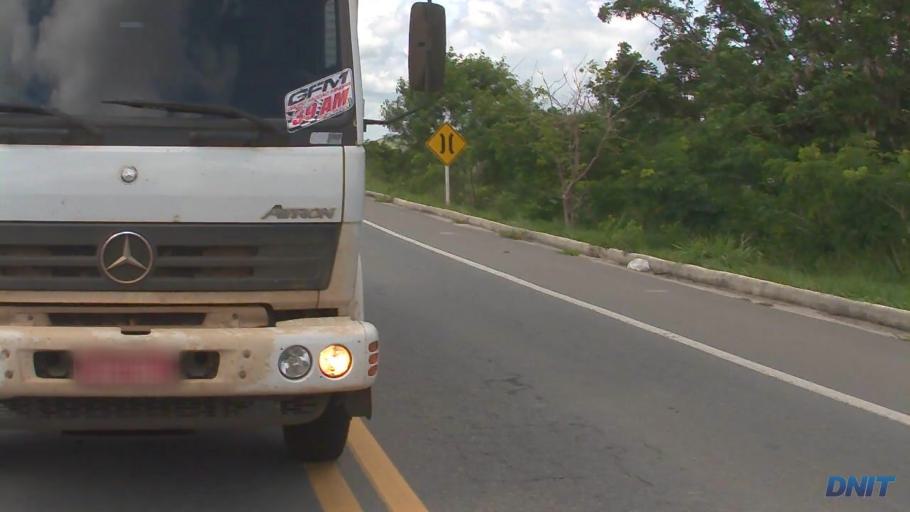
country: BR
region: Minas Gerais
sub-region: Governador Valadares
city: Governador Valadares
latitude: -19.0466
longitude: -42.1541
